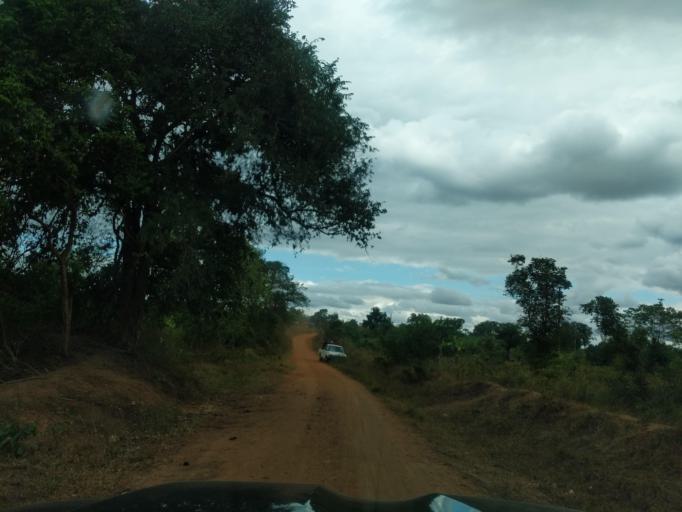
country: TZ
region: Pwani
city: Mvomero
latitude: -5.9408
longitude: 38.4223
